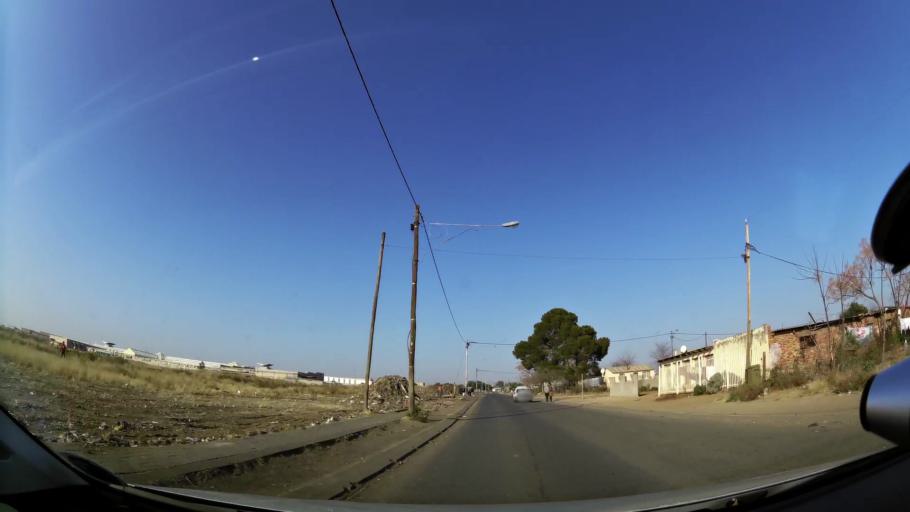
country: ZA
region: Orange Free State
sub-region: Mangaung Metropolitan Municipality
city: Bloemfontein
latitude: -29.1385
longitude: 26.2515
